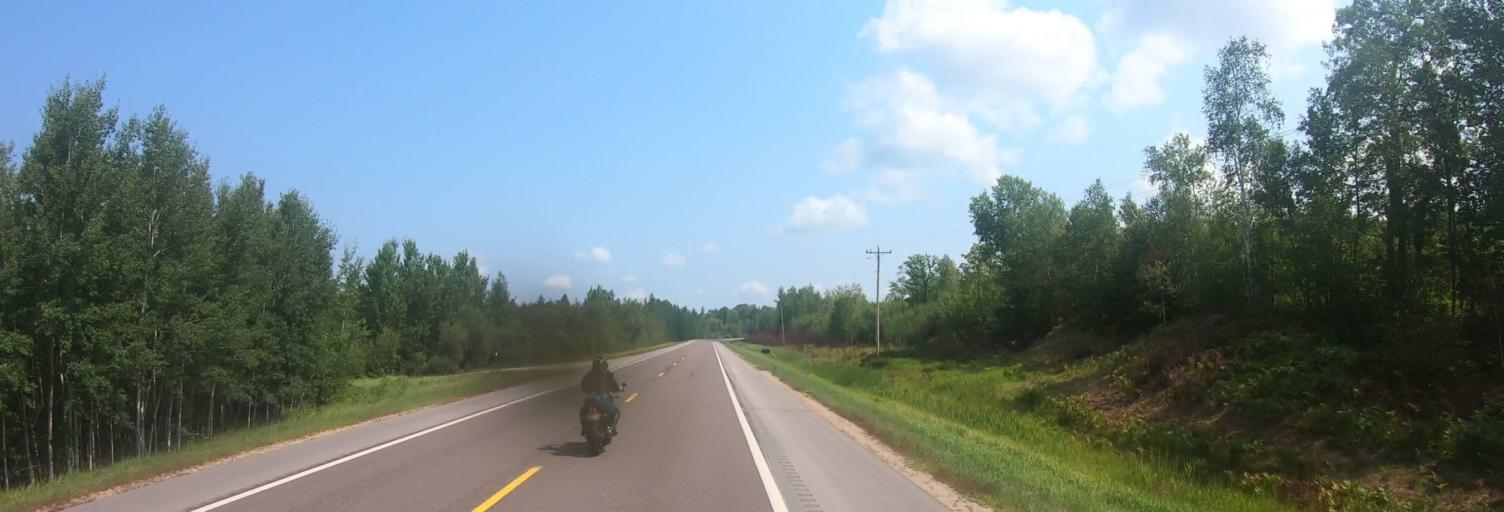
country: US
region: Minnesota
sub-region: Saint Louis County
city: Mountain Iron
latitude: 48.0537
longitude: -92.8015
